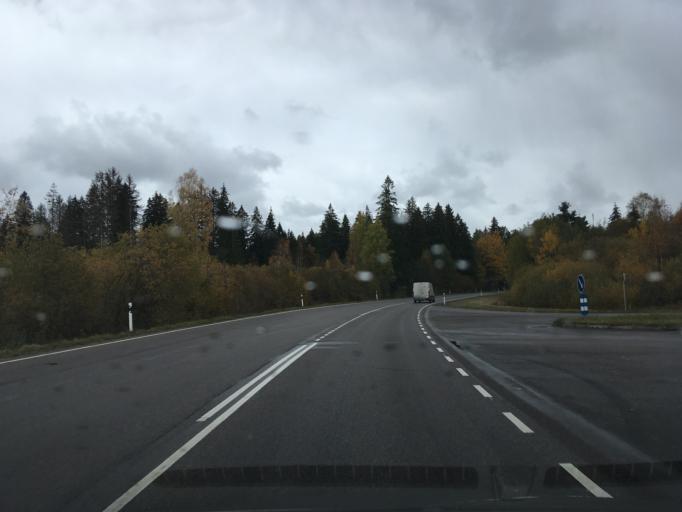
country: EE
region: Harju
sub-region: Anija vald
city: Kehra
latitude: 59.3404
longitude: 25.3095
